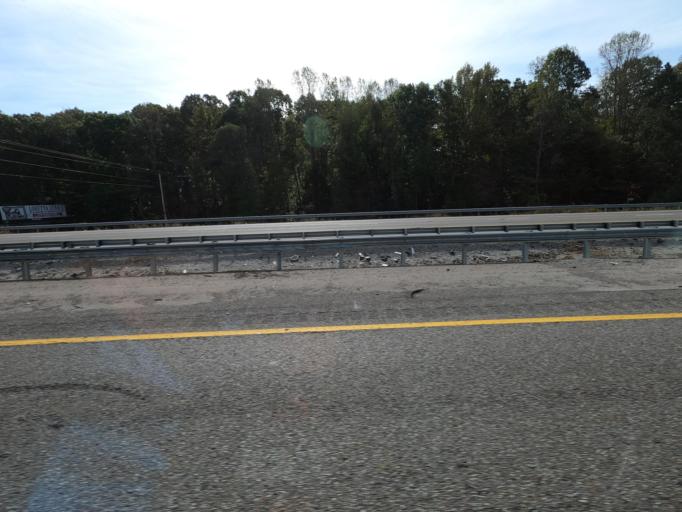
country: US
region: Tennessee
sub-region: Humphreys County
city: New Johnsonville
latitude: 35.8688
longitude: -87.8682
